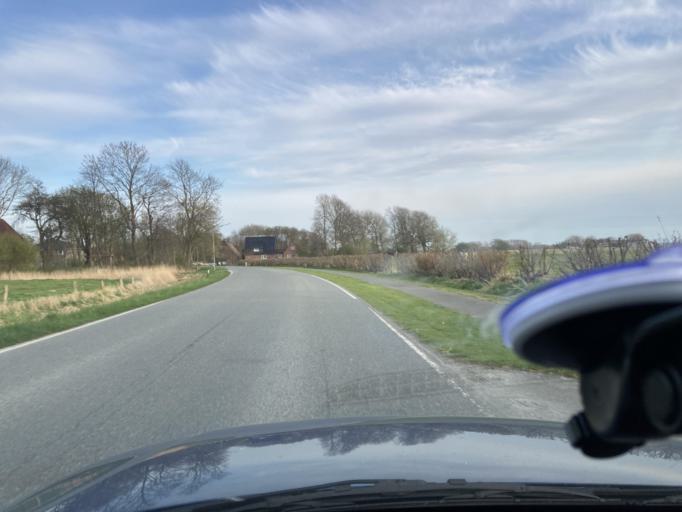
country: DE
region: Schleswig-Holstein
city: Strubbel
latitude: 54.2625
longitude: 8.9684
